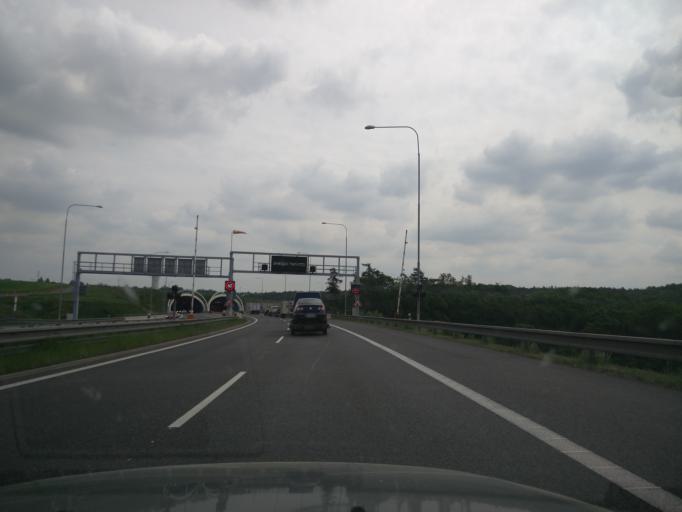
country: CZ
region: Central Bohemia
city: Cernosice
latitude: 49.9986
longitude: 14.3515
